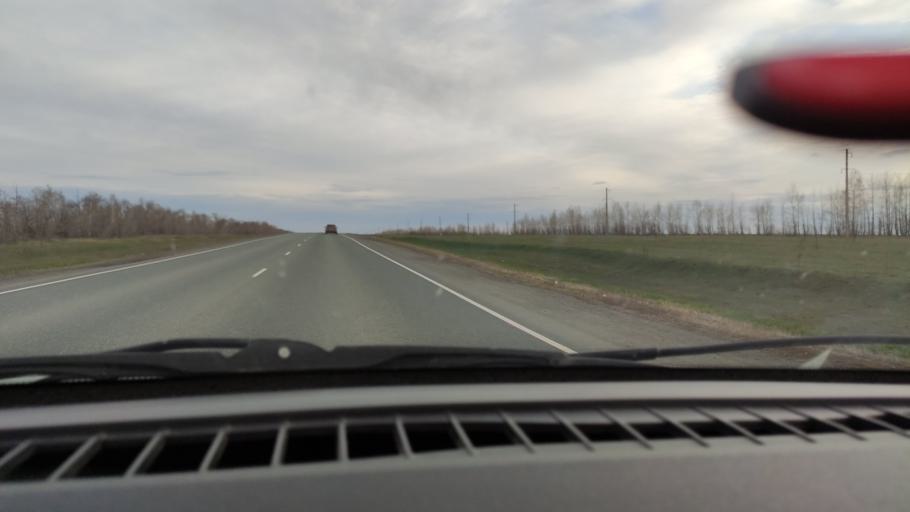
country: RU
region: Orenburg
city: Sakmara
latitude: 52.1412
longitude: 55.2838
